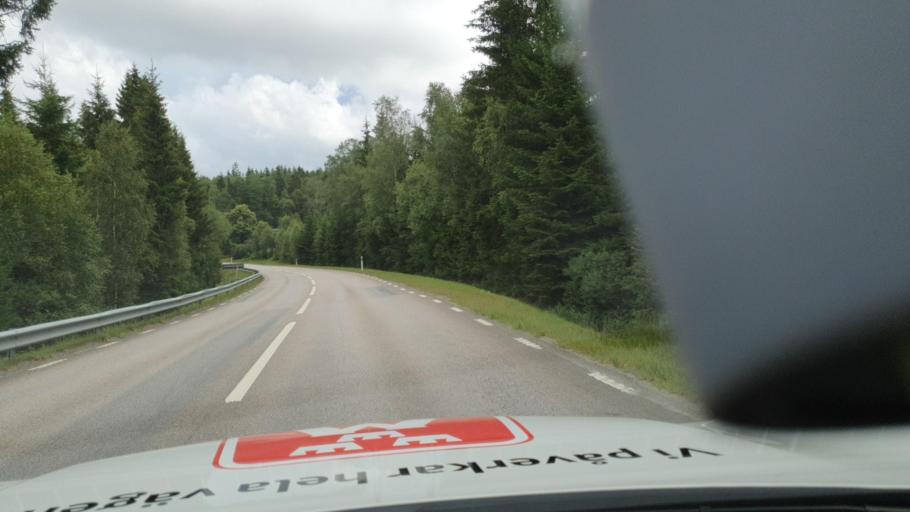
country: SE
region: Vaestra Goetaland
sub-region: Harryda Kommun
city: Hindas
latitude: 57.6976
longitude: 12.4043
